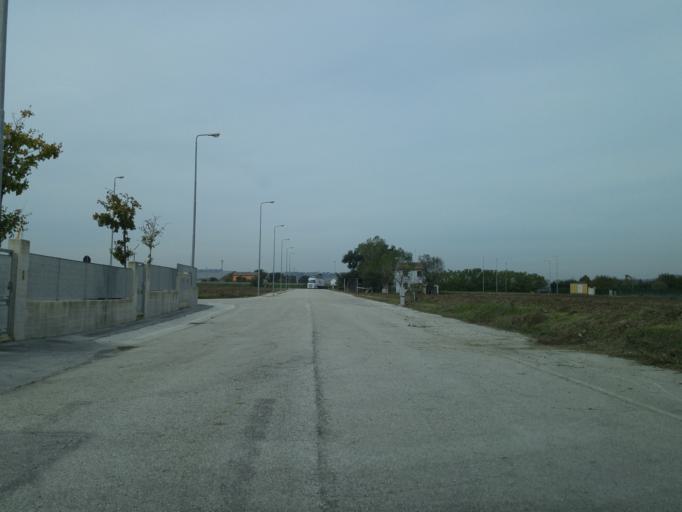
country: IT
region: The Marches
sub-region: Provincia di Pesaro e Urbino
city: Cuccurano
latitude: 43.7688
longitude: 12.9648
